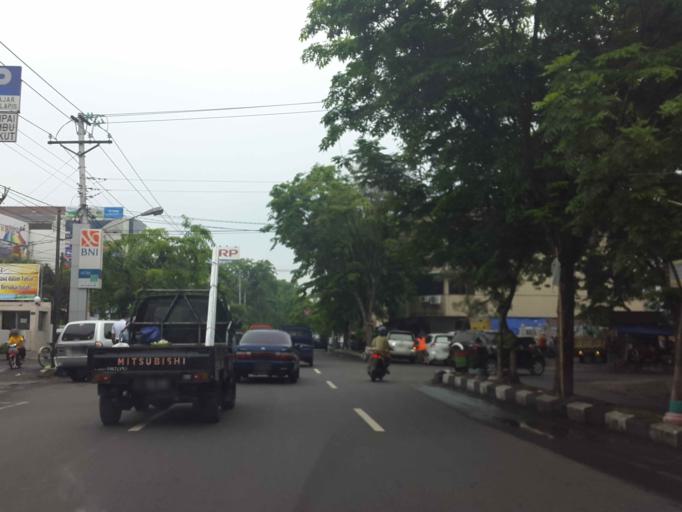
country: ID
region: Central Java
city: Semarang
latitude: -6.9896
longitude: 110.4318
